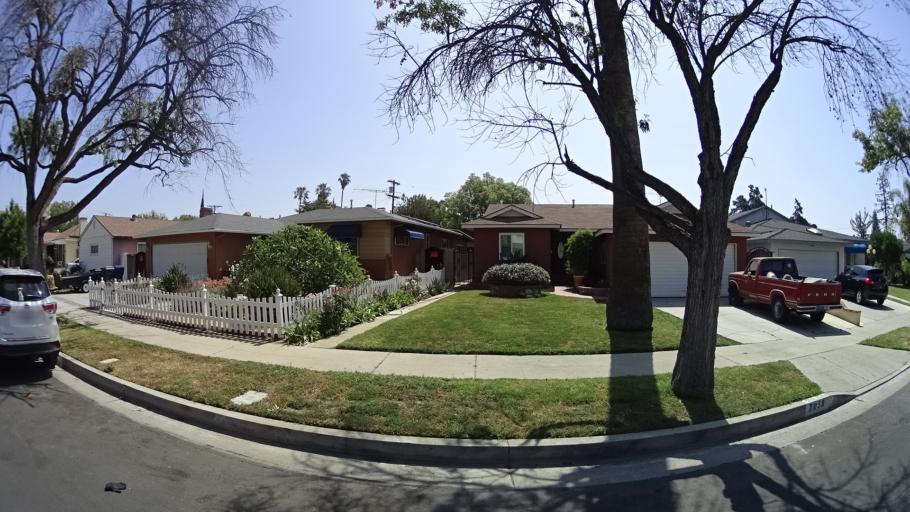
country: US
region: California
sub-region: Los Angeles County
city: Van Nuys
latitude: 34.1991
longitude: -118.4564
